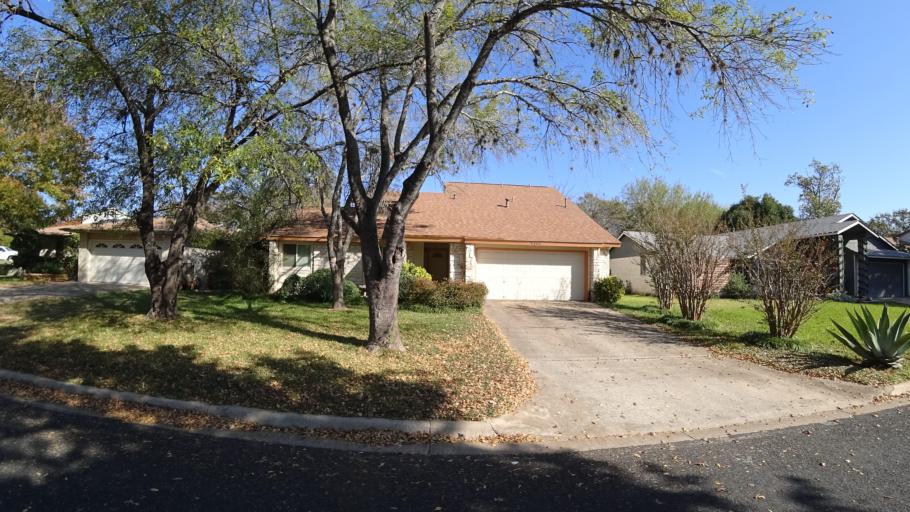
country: US
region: Texas
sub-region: Travis County
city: Barton Creek
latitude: 30.2302
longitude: -97.8518
